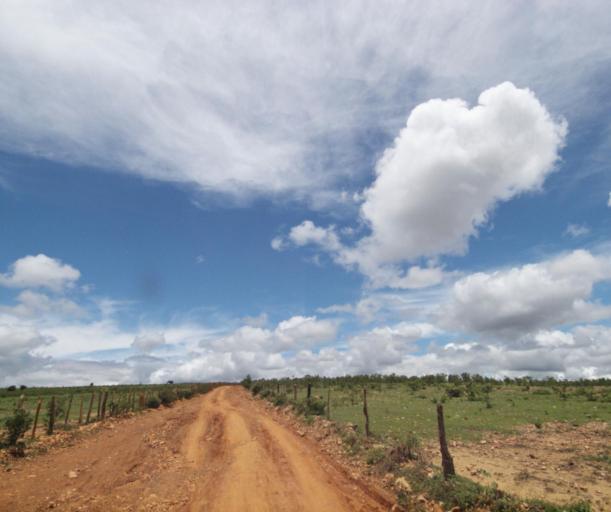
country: BR
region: Bahia
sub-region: Tanhacu
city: Tanhacu
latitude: -14.1924
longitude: -41.0607
